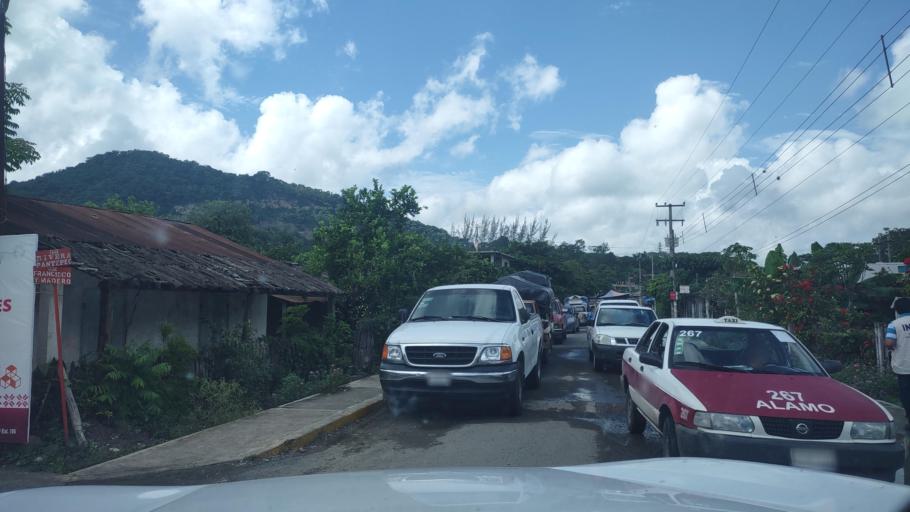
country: MX
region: Veracruz
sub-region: Alamo Temapache
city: Vegas de la Soledad y Soledad Dos
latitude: 20.8929
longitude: -97.7881
